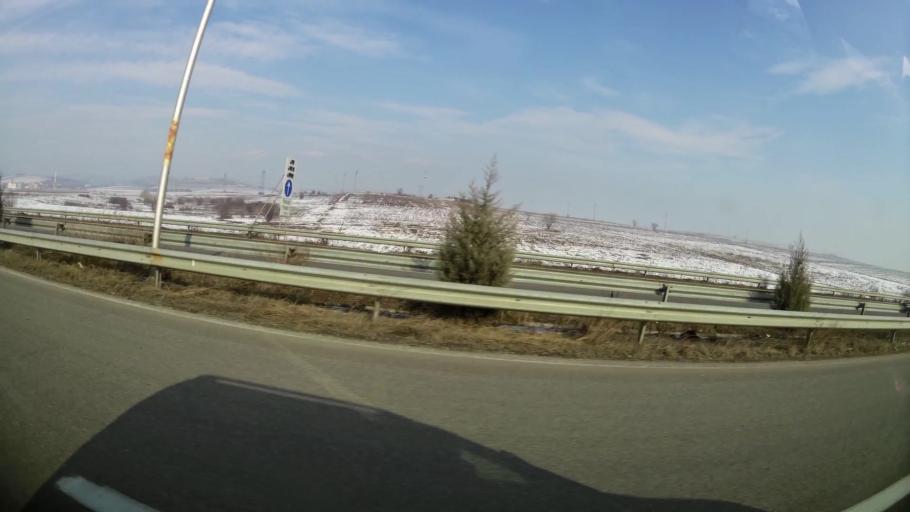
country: MK
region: Butel
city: Butel
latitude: 42.0351
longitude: 21.4702
